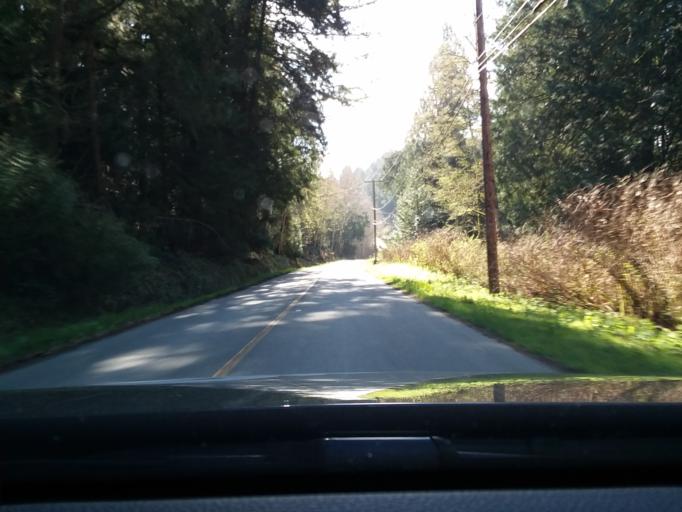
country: CA
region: British Columbia
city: North Cowichan
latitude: 48.9433
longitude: -123.5024
